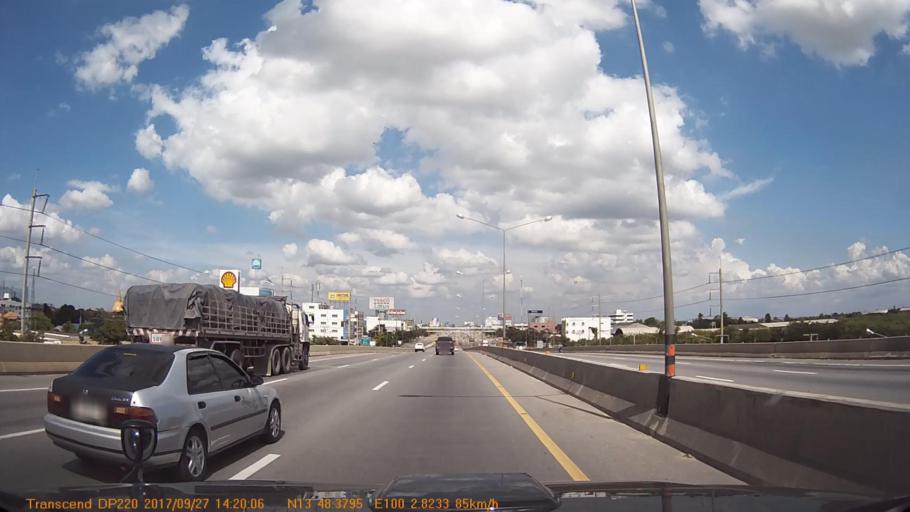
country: TH
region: Nakhon Pathom
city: Nakhon Pathom
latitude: 13.8063
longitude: 100.0468
